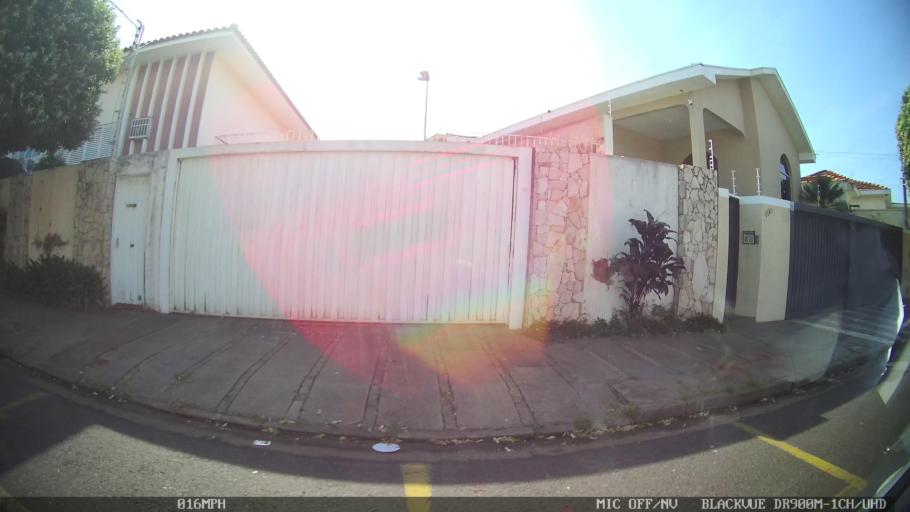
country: BR
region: Sao Paulo
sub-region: Sao Jose Do Rio Preto
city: Sao Jose do Rio Preto
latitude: -20.8068
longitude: -49.3899
